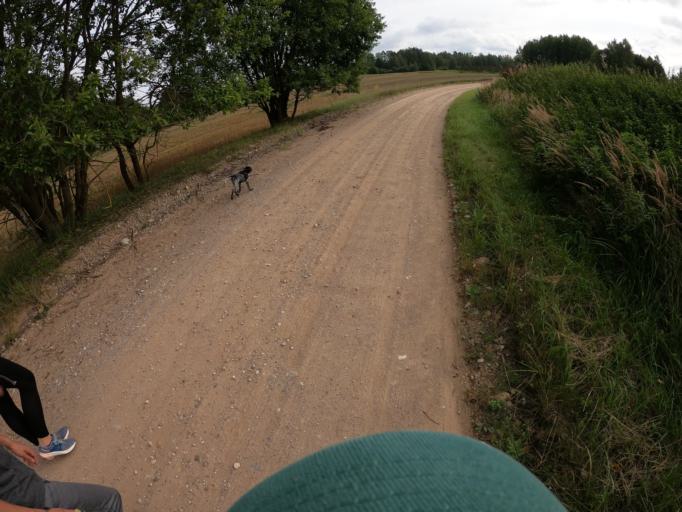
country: LV
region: Tukuma Rajons
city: Tukums
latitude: 56.9851
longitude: 22.9765
